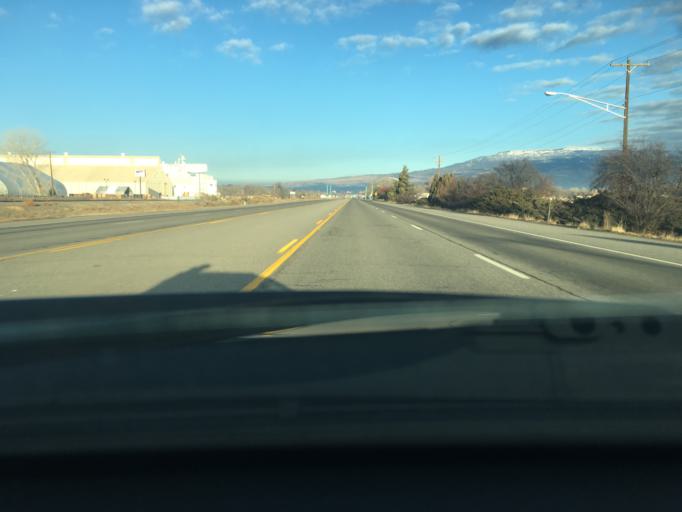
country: US
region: Colorado
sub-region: Delta County
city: Delta
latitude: 38.7218
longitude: -108.0603
